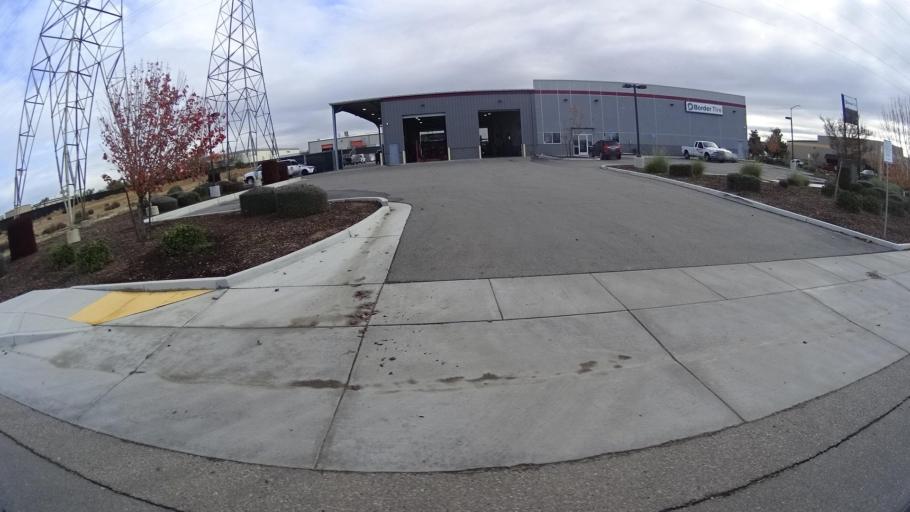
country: US
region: California
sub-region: Kern County
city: Oildale
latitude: 35.4491
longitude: -119.0828
